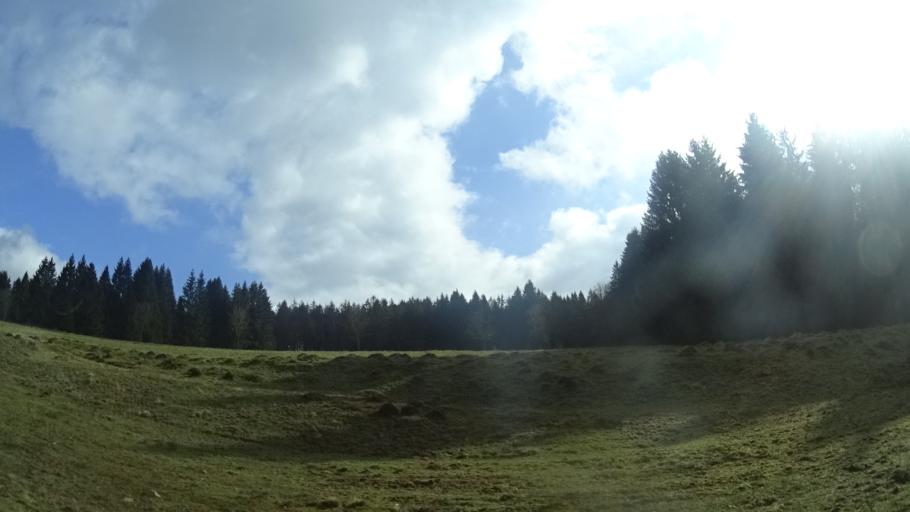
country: DE
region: Rheinland-Pfalz
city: Borfink
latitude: 49.7073
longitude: 7.1016
